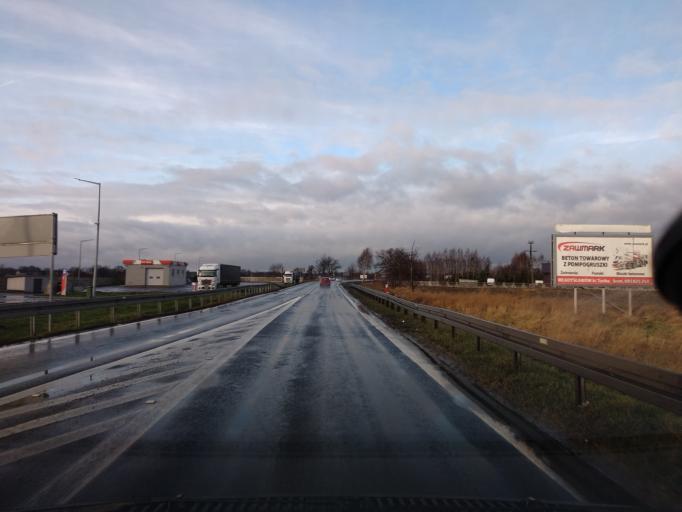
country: PL
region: Greater Poland Voivodeship
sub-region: Powiat koninski
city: Rychwal
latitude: 52.0682
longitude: 18.1613
